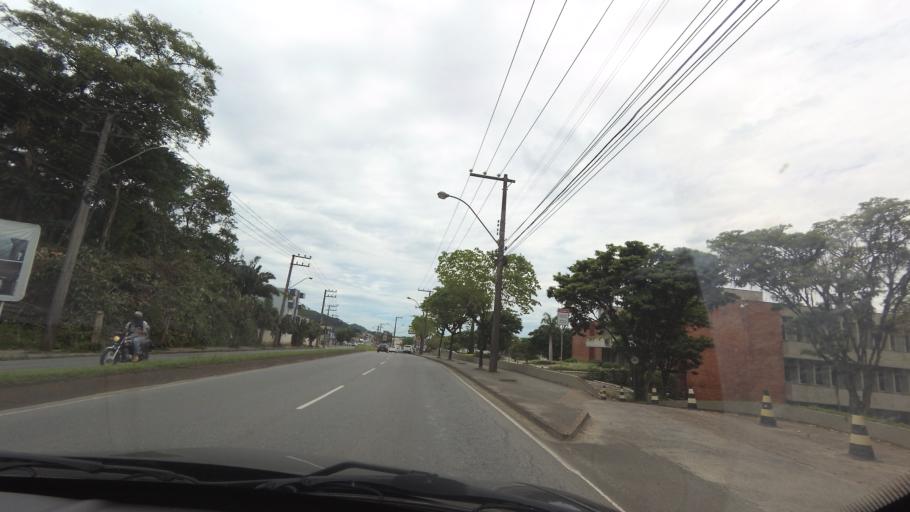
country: BR
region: Santa Catarina
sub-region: Jaragua Do Sul
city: Jaragua do Sul
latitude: -26.4781
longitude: -49.0508
